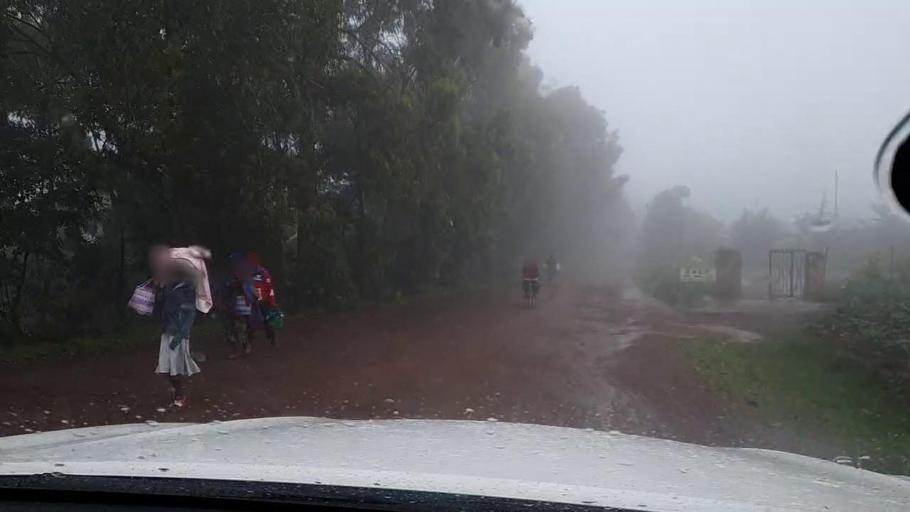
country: RW
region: Kigali
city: Kigali
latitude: -1.7713
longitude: 29.9983
